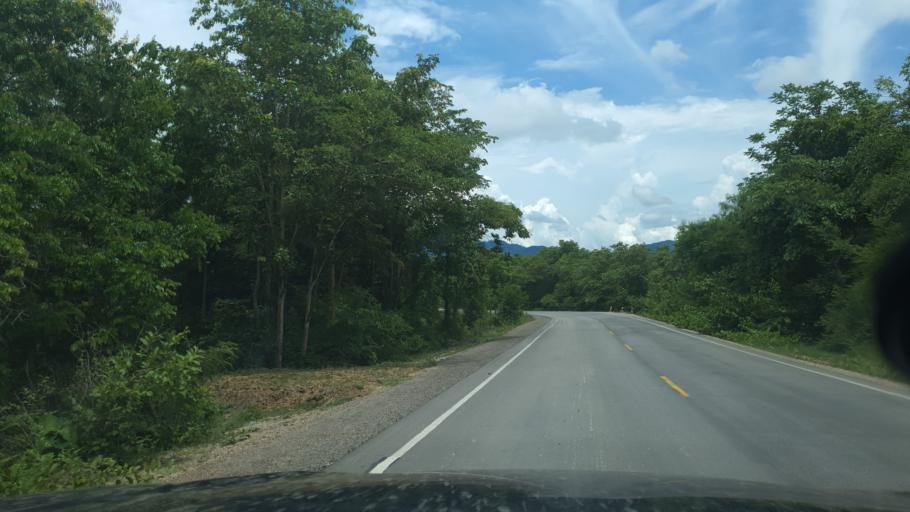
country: TH
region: Lampang
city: Sop Prap
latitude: 17.9304
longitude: 99.3709
